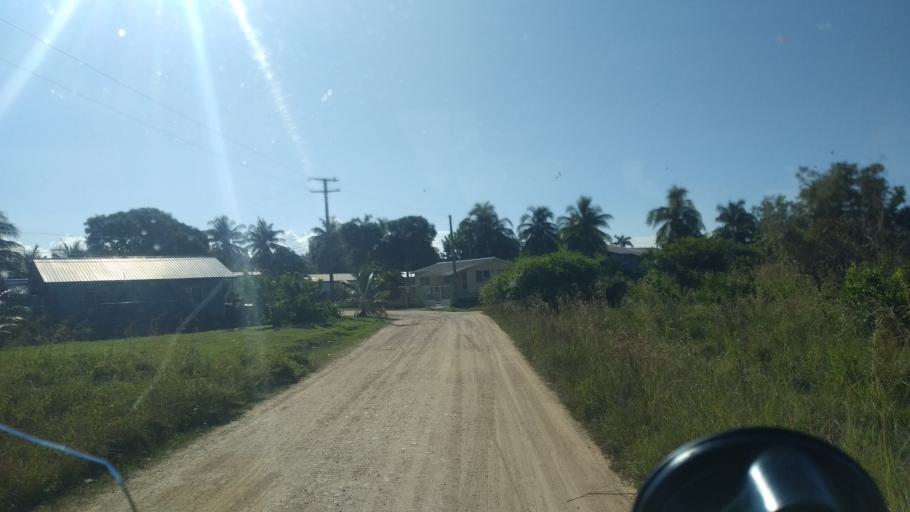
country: BZ
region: Belize
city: Belize City
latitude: 17.5516
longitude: -88.3261
